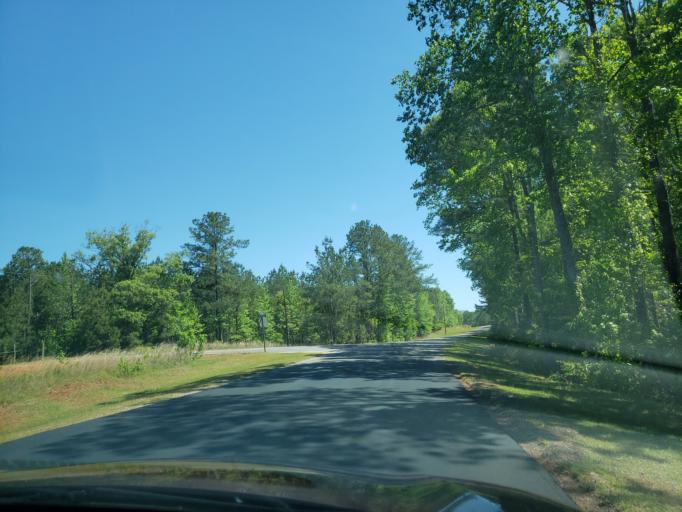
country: US
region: Alabama
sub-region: Elmore County
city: Eclectic
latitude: 32.7027
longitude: -85.8869
